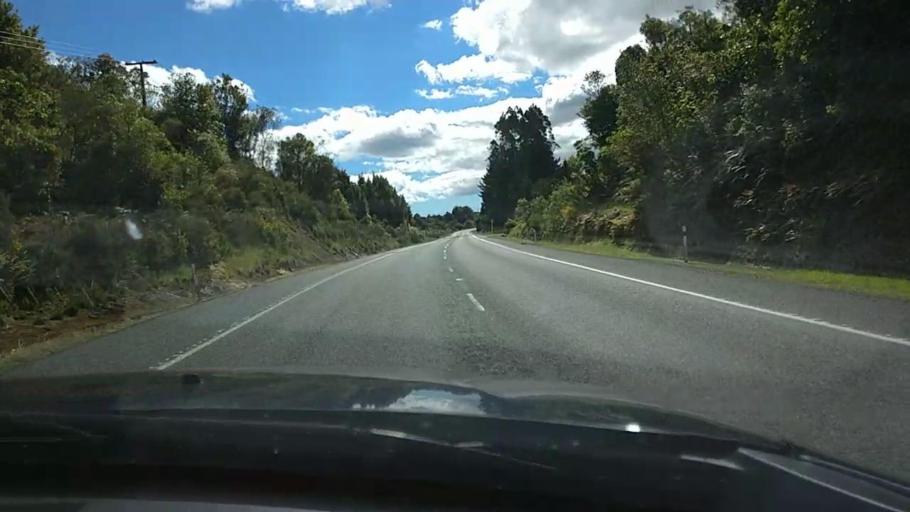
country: NZ
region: Bay of Plenty
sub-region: Rotorua District
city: Rotorua
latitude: -38.0718
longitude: 176.1292
